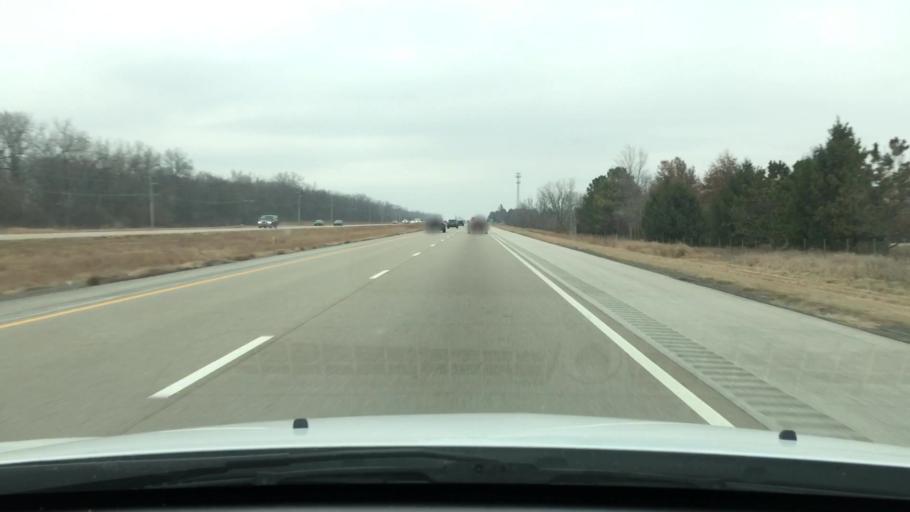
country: US
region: Illinois
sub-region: Logan County
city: Atlanta
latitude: 40.2386
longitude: -89.2567
